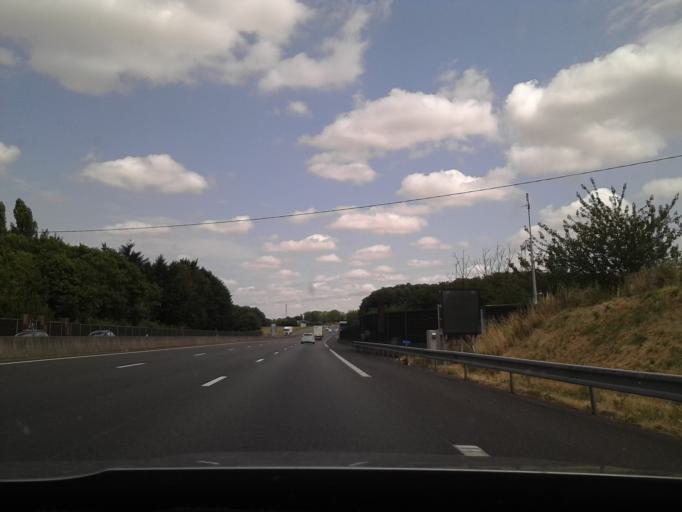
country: FR
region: Centre
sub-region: Departement d'Indre-et-Loire
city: Parcay-Meslay
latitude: 47.4675
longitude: 0.7663
